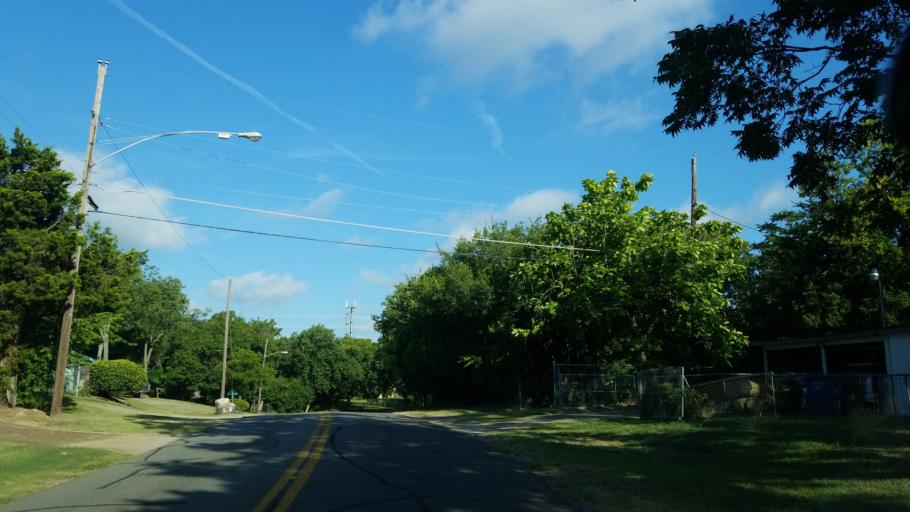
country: US
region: Texas
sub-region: Dallas County
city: Dallas
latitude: 32.7297
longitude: -96.8013
